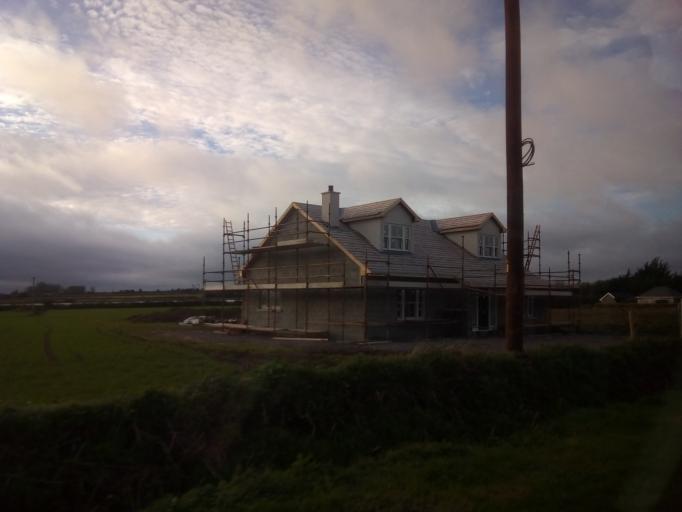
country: IE
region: Leinster
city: Balrothery
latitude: 53.5779
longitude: -6.1580
